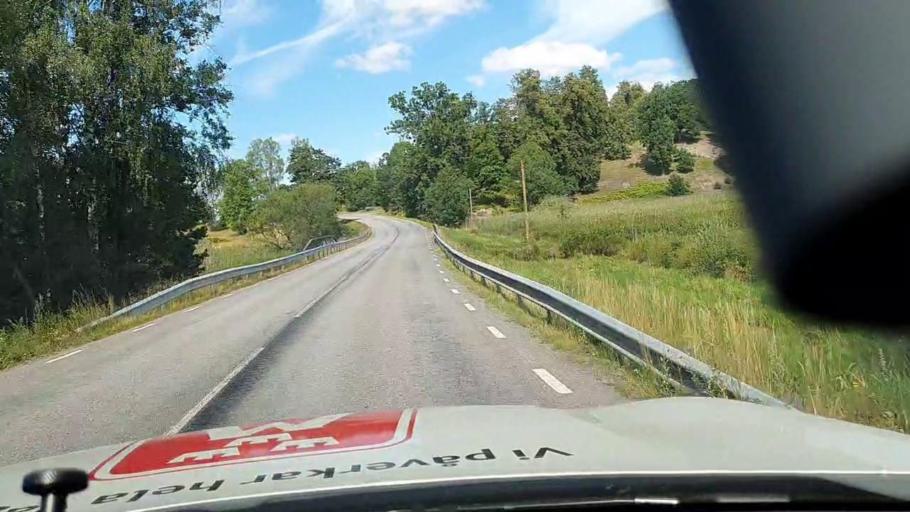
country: SE
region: Soedermanland
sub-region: Strangnas Kommun
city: Akers Styckebruk
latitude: 59.2681
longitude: 16.9821
